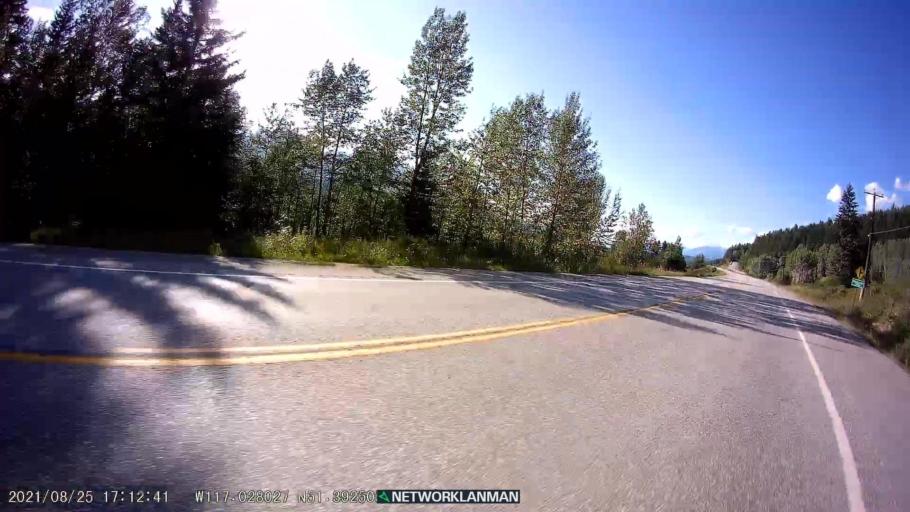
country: CA
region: British Columbia
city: Golden
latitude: 51.3928
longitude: -117.0280
